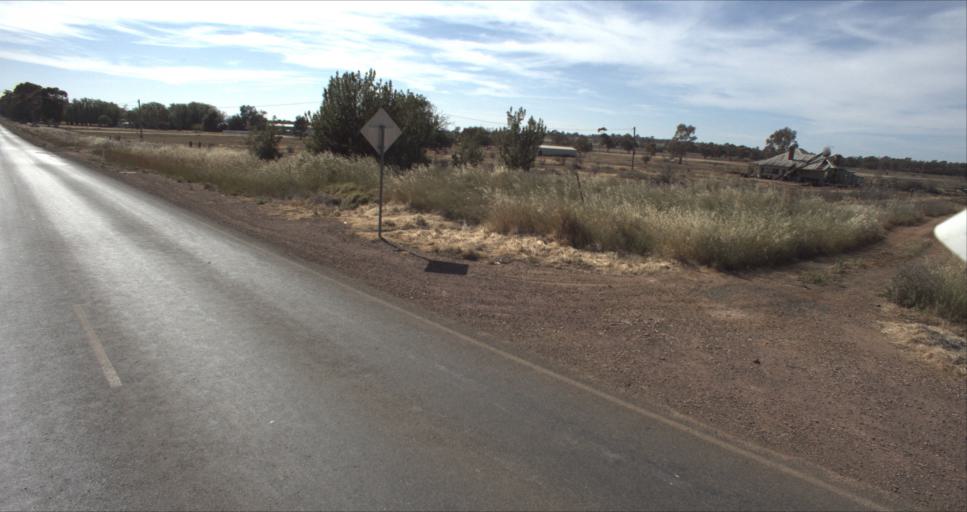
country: AU
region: New South Wales
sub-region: Leeton
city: Leeton
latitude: -34.5642
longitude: 146.4270
